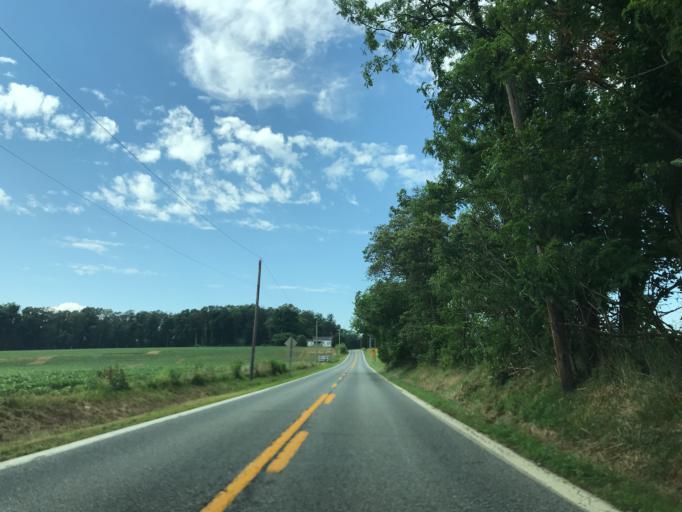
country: US
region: Pennsylvania
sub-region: York County
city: Susquehanna Trails
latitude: 39.7084
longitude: -76.4257
